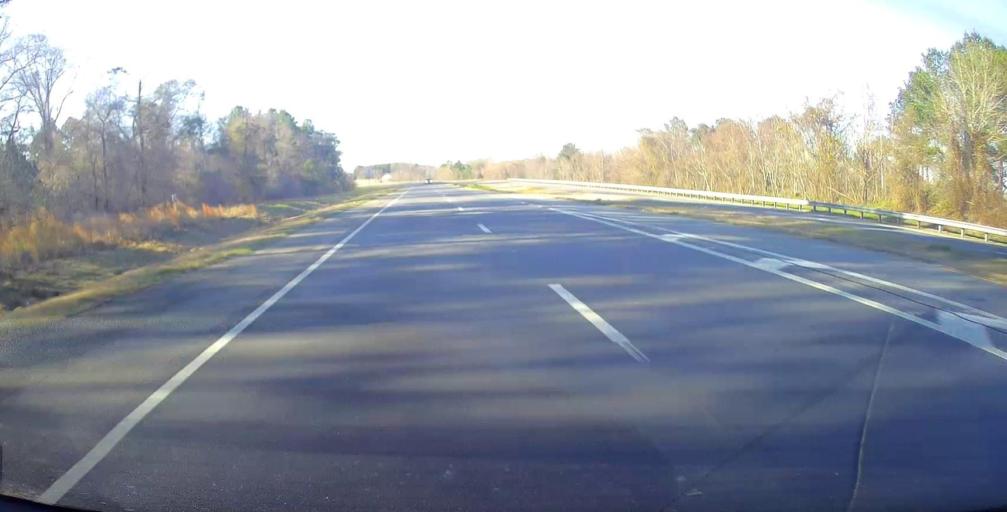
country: US
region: Georgia
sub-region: Lee County
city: Leesburg
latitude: 31.8090
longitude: -84.2086
